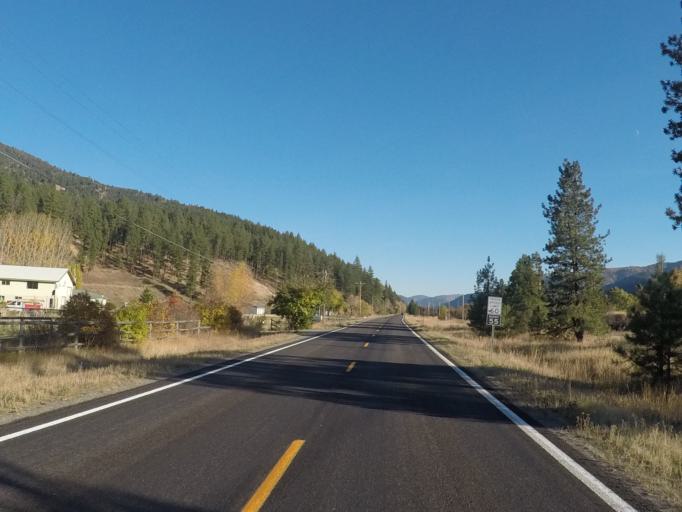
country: US
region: Montana
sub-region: Missoula County
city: Bonner-West Riverside
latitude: 46.8344
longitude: -113.8236
